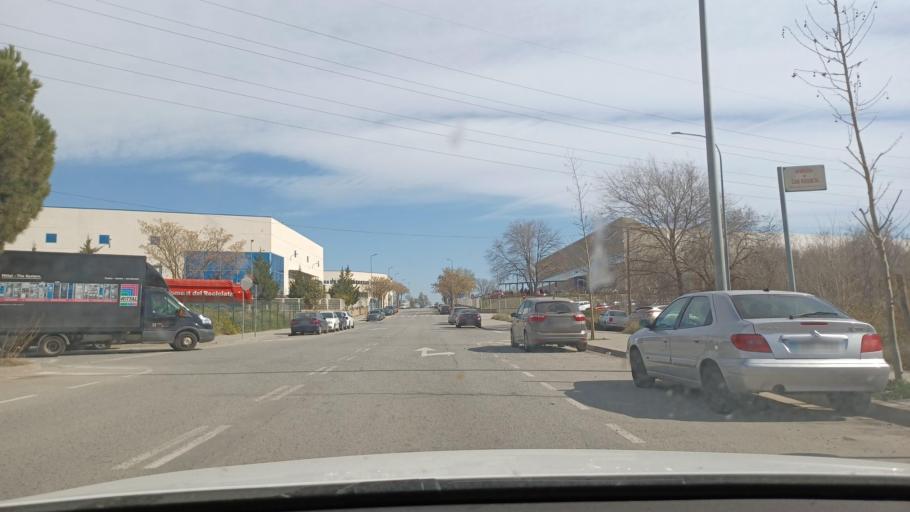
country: ES
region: Catalonia
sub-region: Provincia de Barcelona
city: Polinya
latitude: 41.5376
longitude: 2.1365
